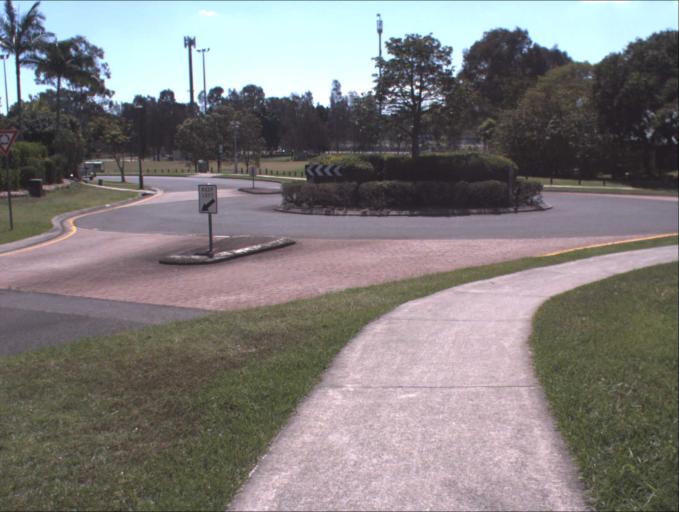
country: AU
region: Queensland
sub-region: Logan
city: Beenleigh
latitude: -27.7000
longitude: 153.1724
